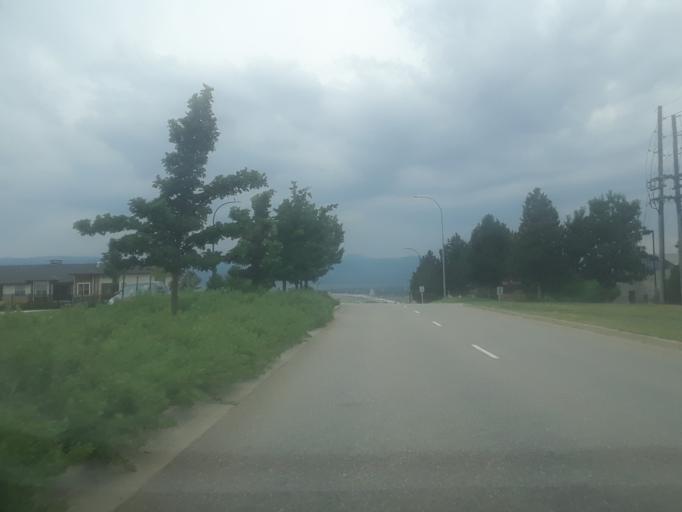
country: US
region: Colorado
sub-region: Arapahoe County
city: Columbine Valley
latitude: 39.5662
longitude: -105.0226
